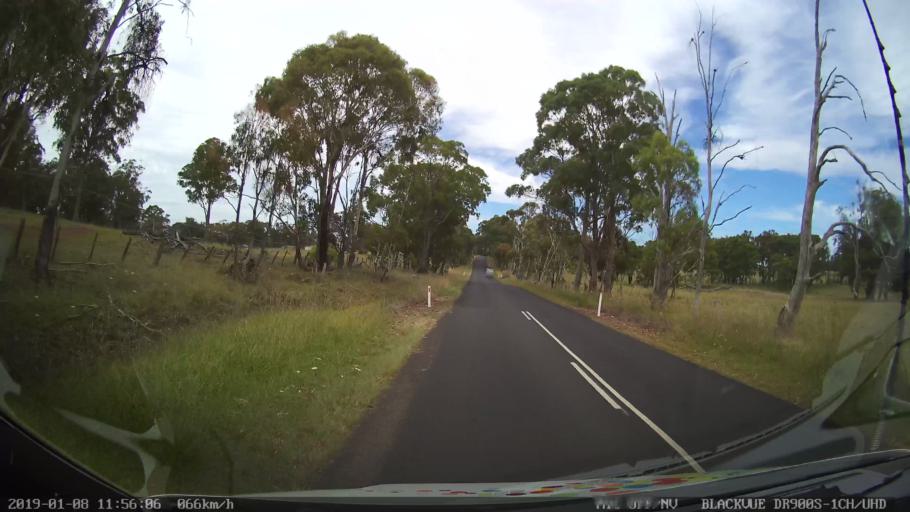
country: AU
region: New South Wales
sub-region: Armidale Dumaresq
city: Armidale
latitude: -30.4364
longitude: 151.5650
